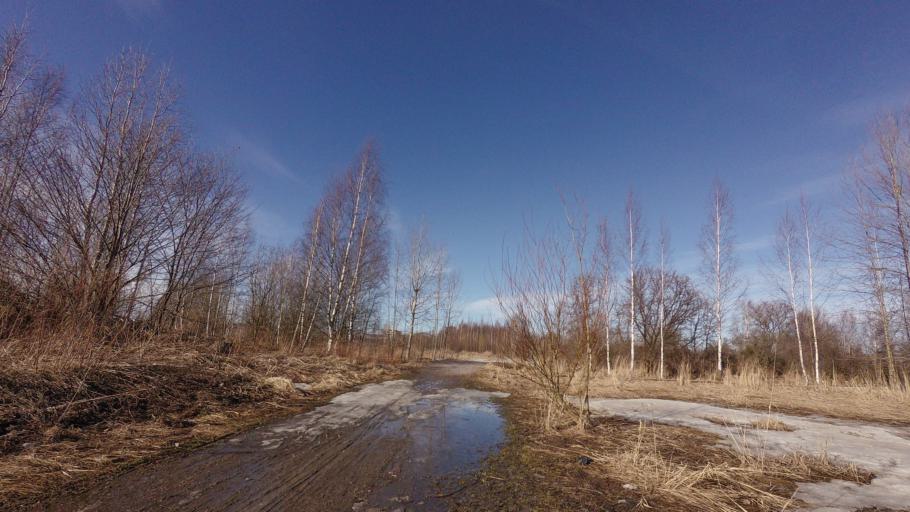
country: FI
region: Uusimaa
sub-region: Helsinki
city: Helsinki
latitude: 60.1988
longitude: 24.9795
